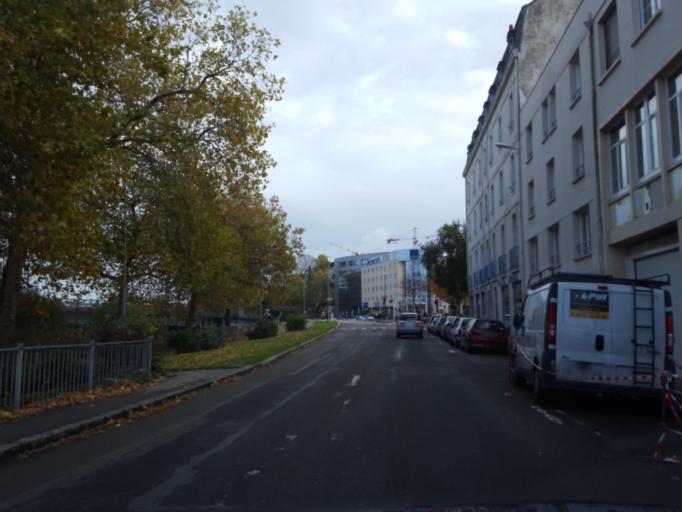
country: FR
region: Pays de la Loire
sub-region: Departement de la Loire-Atlantique
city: Nantes
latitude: 47.2069
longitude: -1.5503
